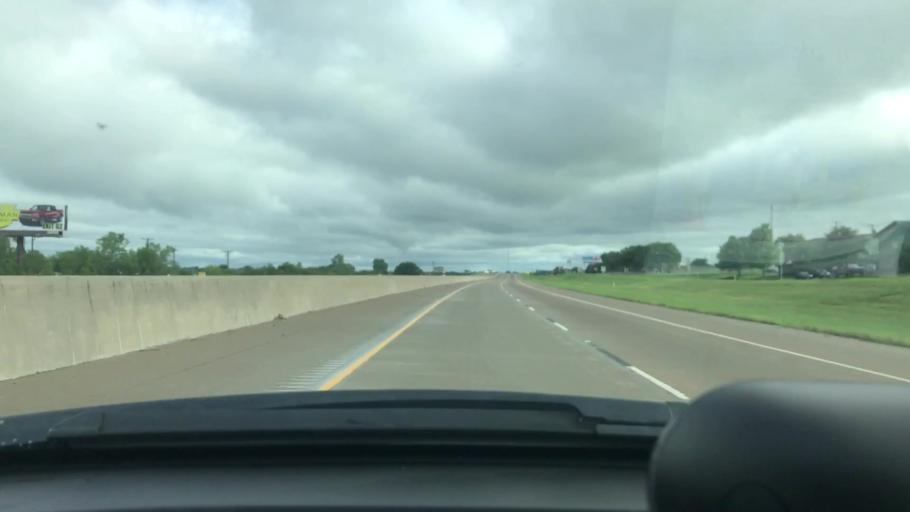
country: US
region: Texas
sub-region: Grayson County
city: Howe
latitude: 33.4997
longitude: -96.6195
